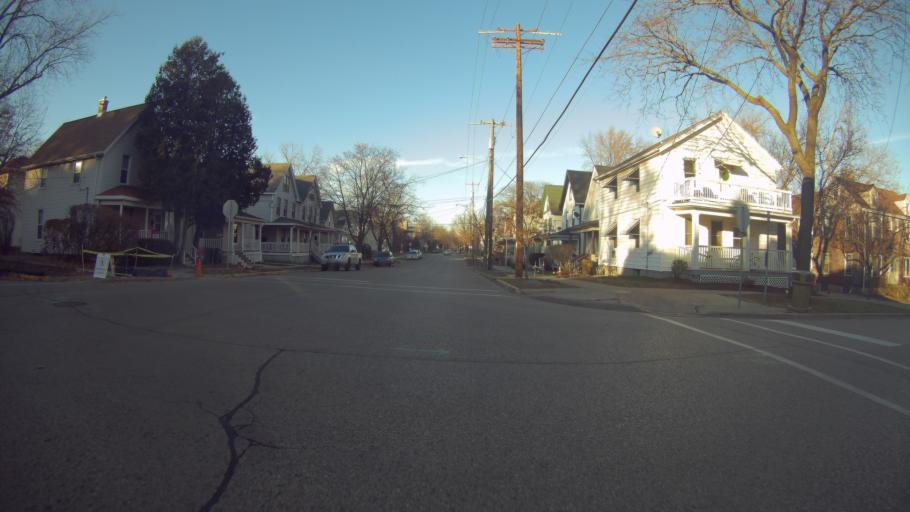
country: US
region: Wisconsin
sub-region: Dane County
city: Madison
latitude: 43.0597
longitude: -89.4040
